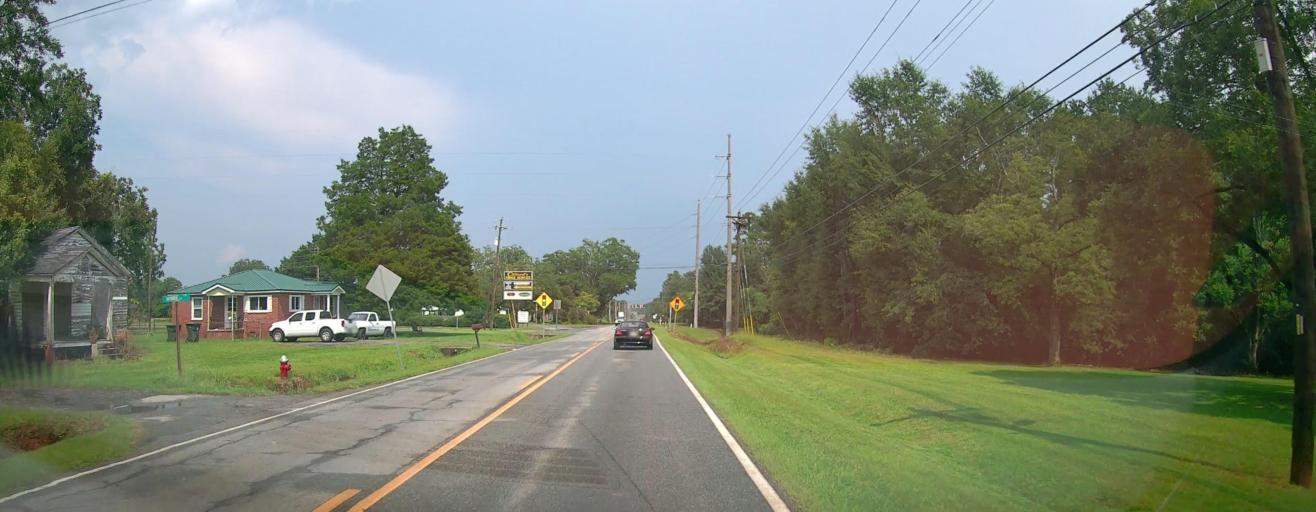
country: US
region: Georgia
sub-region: Houston County
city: Centerville
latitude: 32.6508
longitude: -83.6439
